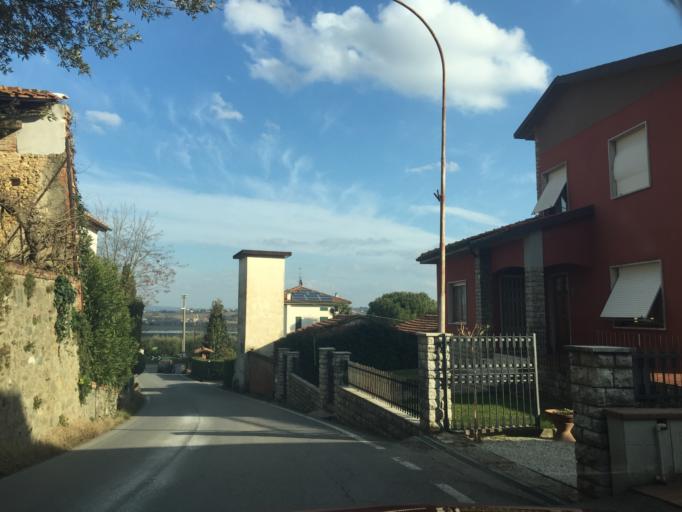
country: IT
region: Tuscany
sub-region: Province of Florence
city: Stabbia
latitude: 43.7803
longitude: 10.8006
